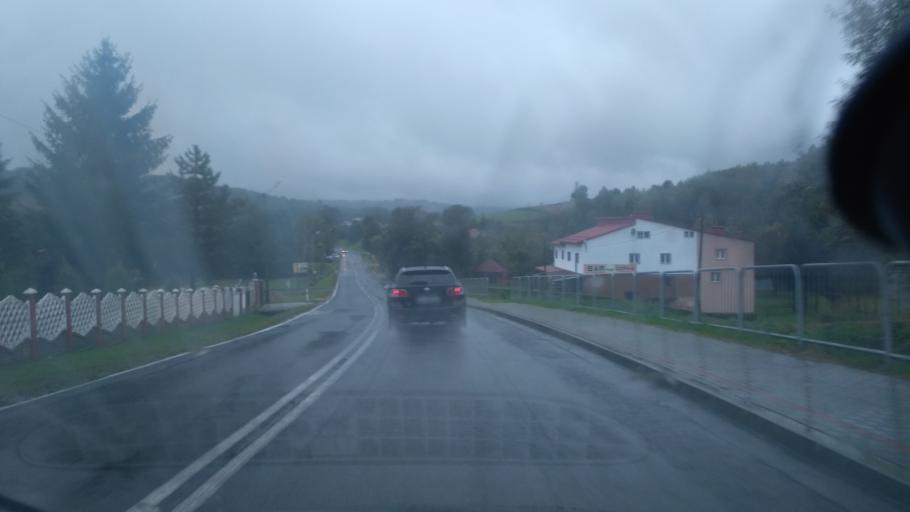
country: PL
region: Subcarpathian Voivodeship
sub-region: Powiat ropczycko-sedziszowski
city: Niedzwiada
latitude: 50.0030
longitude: 21.5596
